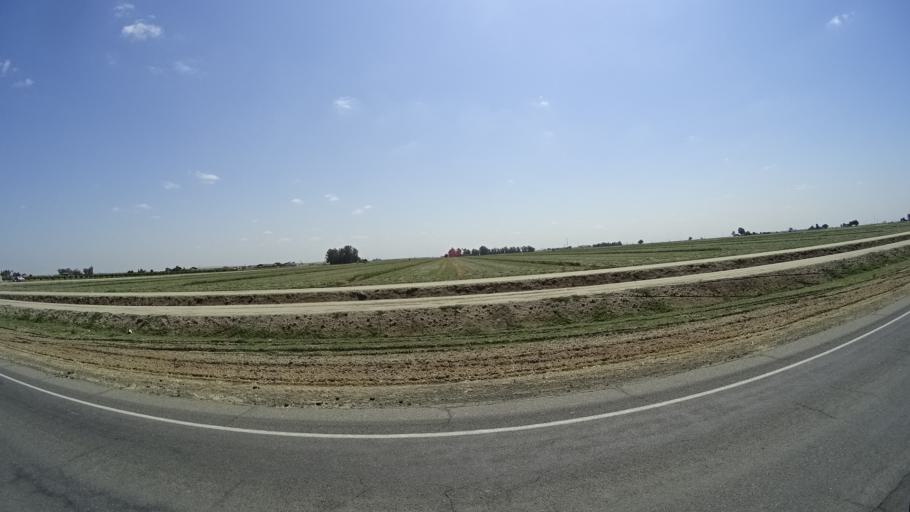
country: US
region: California
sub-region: Kings County
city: Home Garden
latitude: 36.2173
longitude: -119.6369
